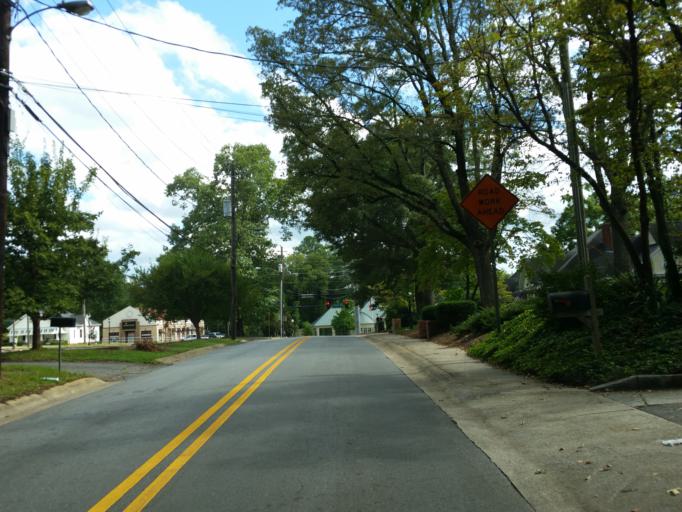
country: US
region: Georgia
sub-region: Cobb County
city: Smyrna
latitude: 33.8814
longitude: -84.5164
